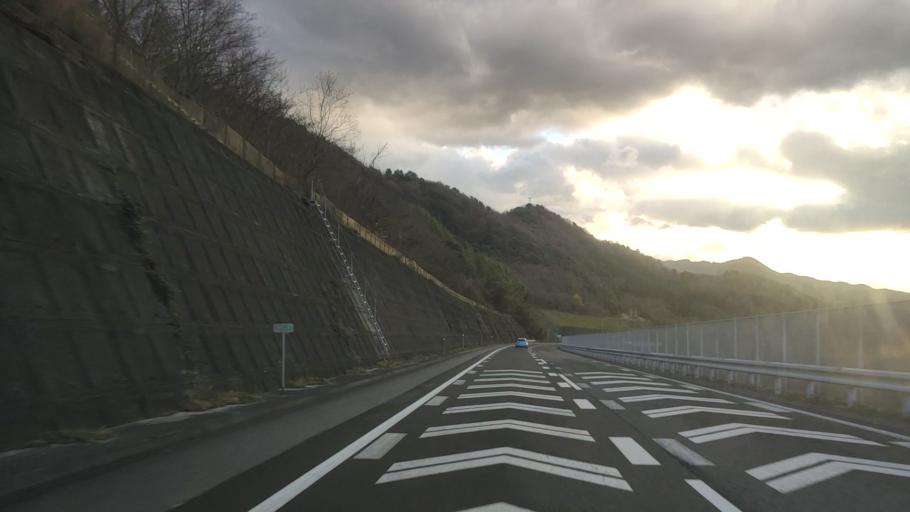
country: JP
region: Ehime
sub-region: Shikoku-chuo Shi
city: Matsuyama
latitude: 33.8066
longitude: 132.9445
